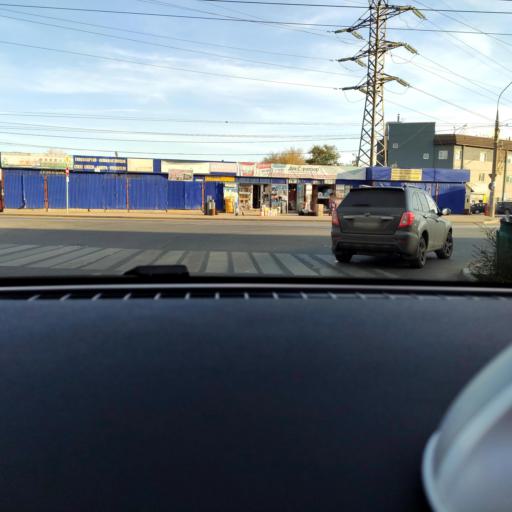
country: RU
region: Samara
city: Petra-Dubrava
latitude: 53.2282
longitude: 50.2814
